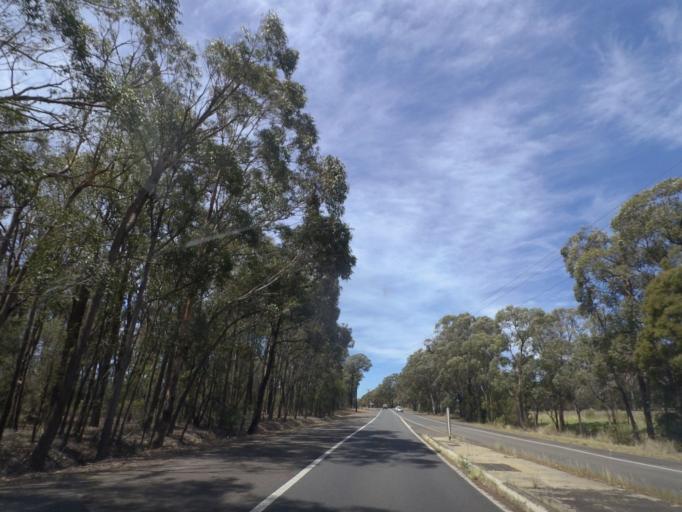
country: AU
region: New South Wales
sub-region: Wollondilly
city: Buxton
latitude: -34.3138
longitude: 150.5838
